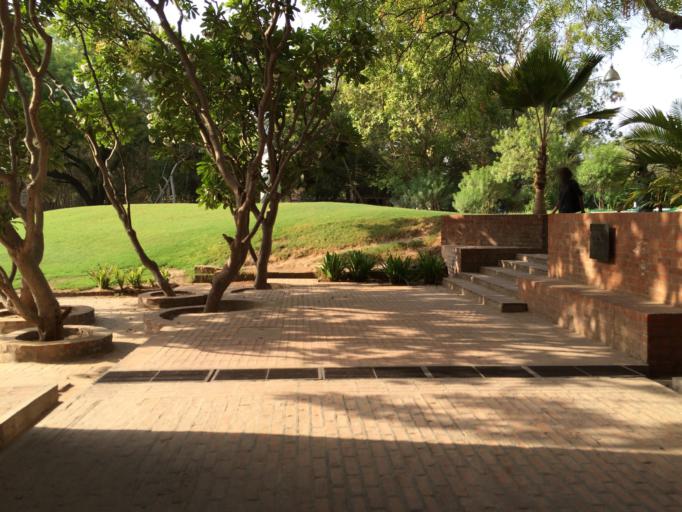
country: IN
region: Gujarat
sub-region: Ahmadabad
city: Ahmedabad
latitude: 23.0380
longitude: 72.5500
